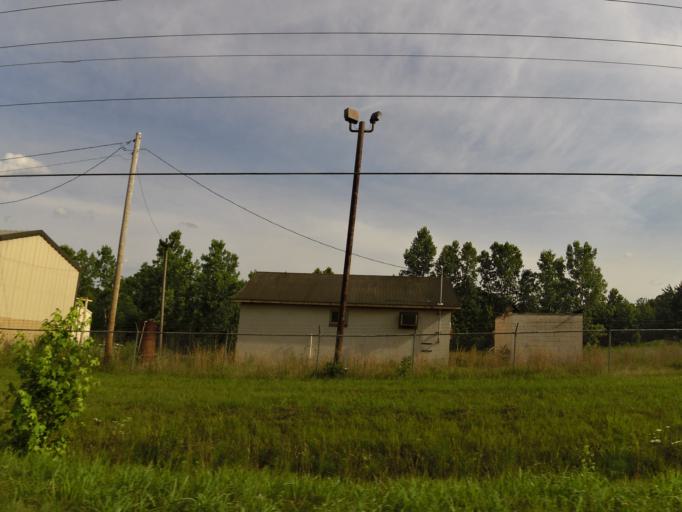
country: US
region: Tennessee
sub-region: Benton County
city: Camden
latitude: 36.0452
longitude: -88.1472
